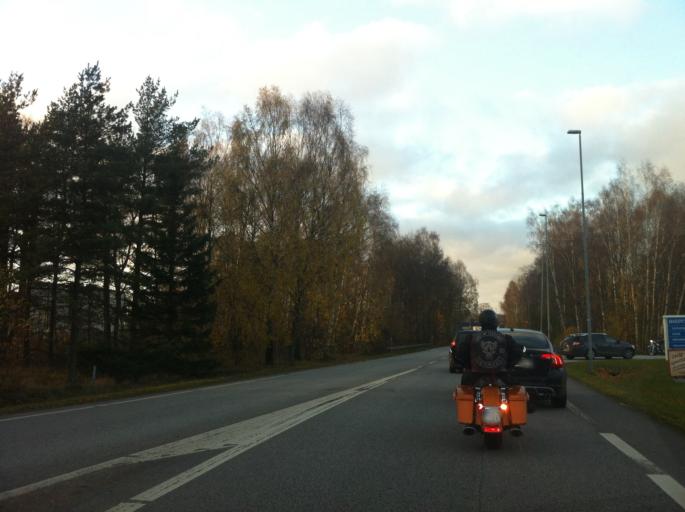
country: SE
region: Skane
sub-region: Hoors Kommun
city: Hoeoer
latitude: 55.9403
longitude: 13.5591
